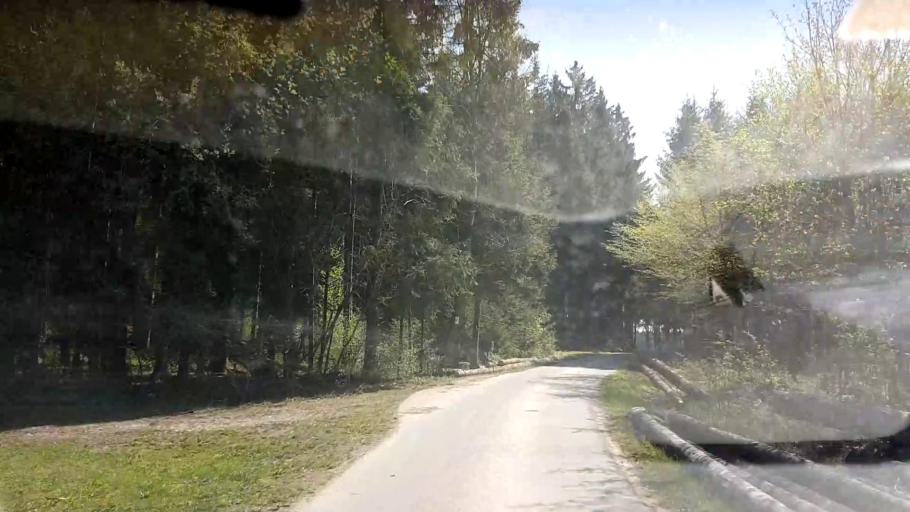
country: DE
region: Bavaria
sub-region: Upper Franconia
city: Konigsfeld
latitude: 49.9238
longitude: 11.1749
